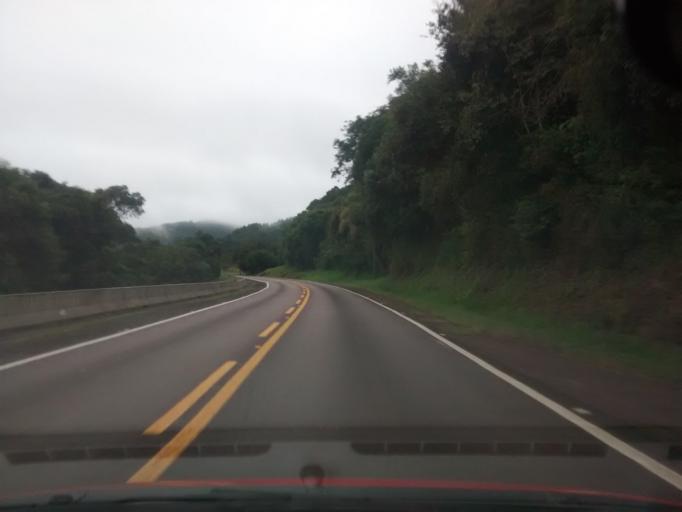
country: BR
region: Rio Grande do Sul
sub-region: Vacaria
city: Estrela
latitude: -28.1982
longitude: -50.7513
